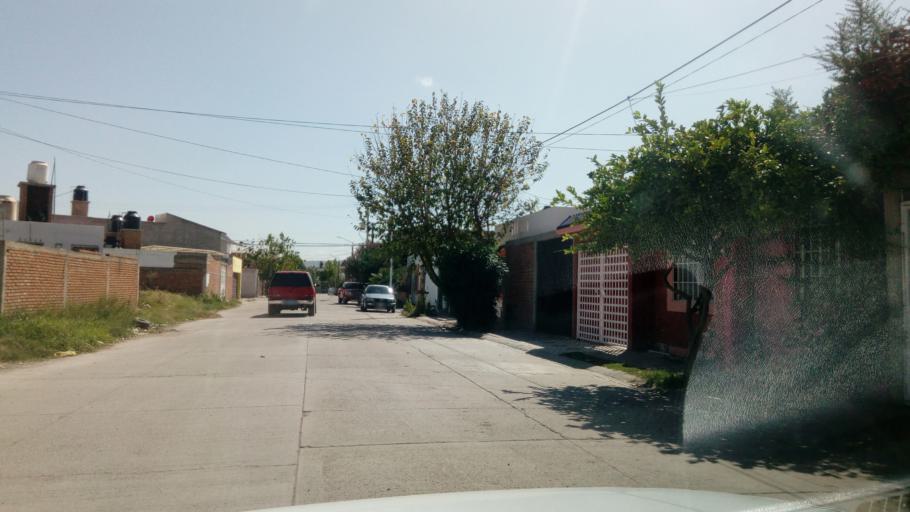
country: MX
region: Durango
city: Victoria de Durango
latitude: 23.9937
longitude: -104.6933
